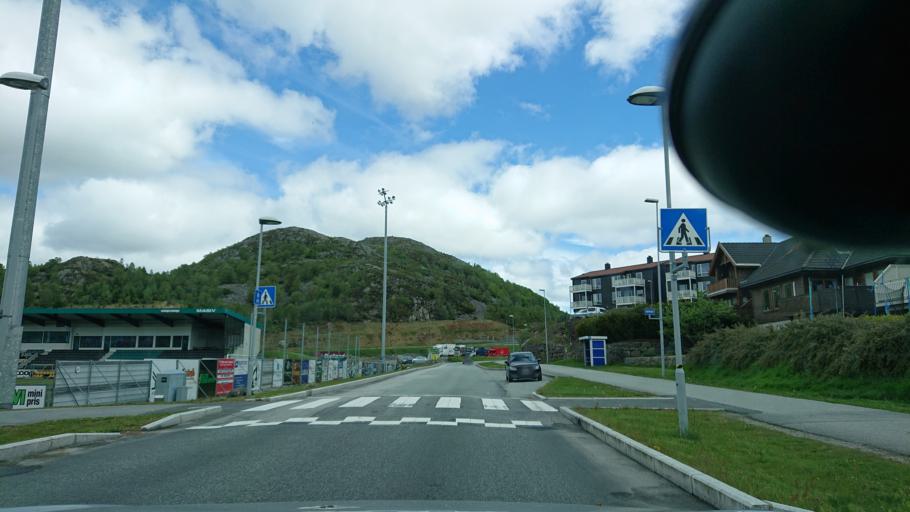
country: NO
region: Rogaland
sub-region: Gjesdal
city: Algard
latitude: 58.7744
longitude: 5.8678
